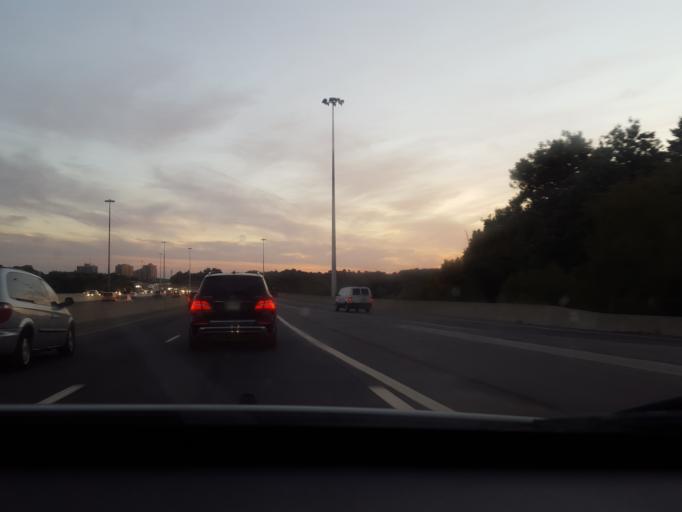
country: CA
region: Ontario
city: North York
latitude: 43.7532
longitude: -79.4094
